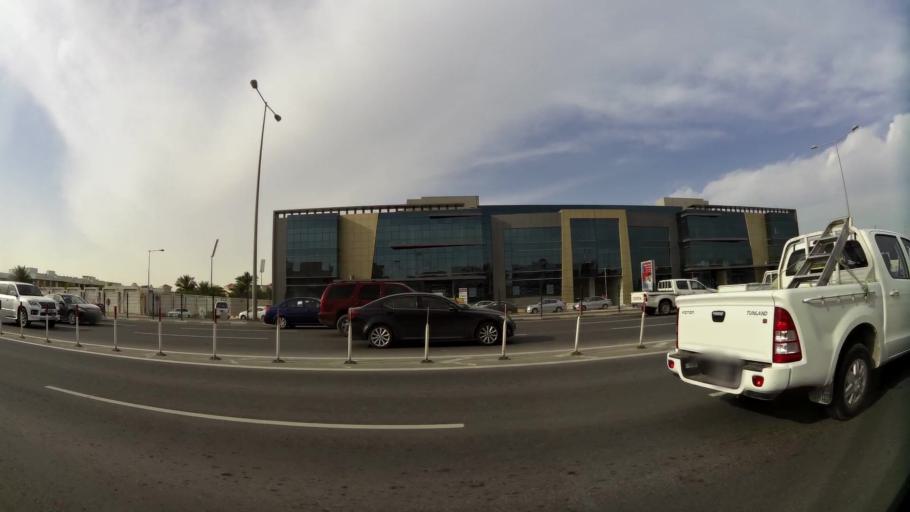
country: QA
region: Baladiyat ad Dawhah
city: Doha
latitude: 25.2542
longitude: 51.5222
